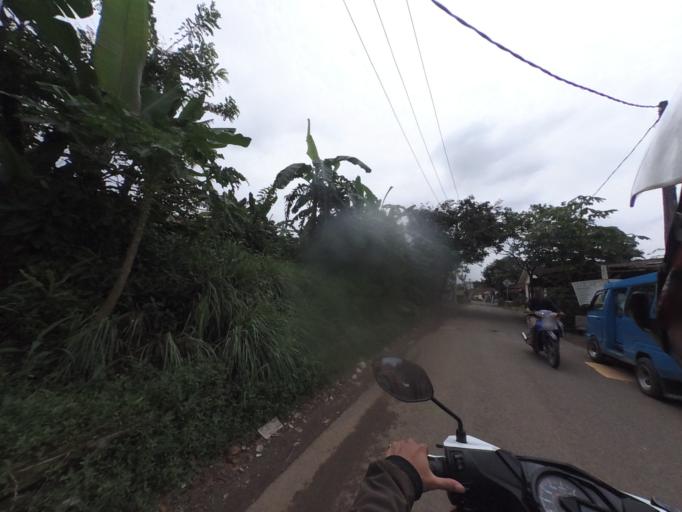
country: ID
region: West Java
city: Bogor
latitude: -6.6111
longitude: 106.7527
